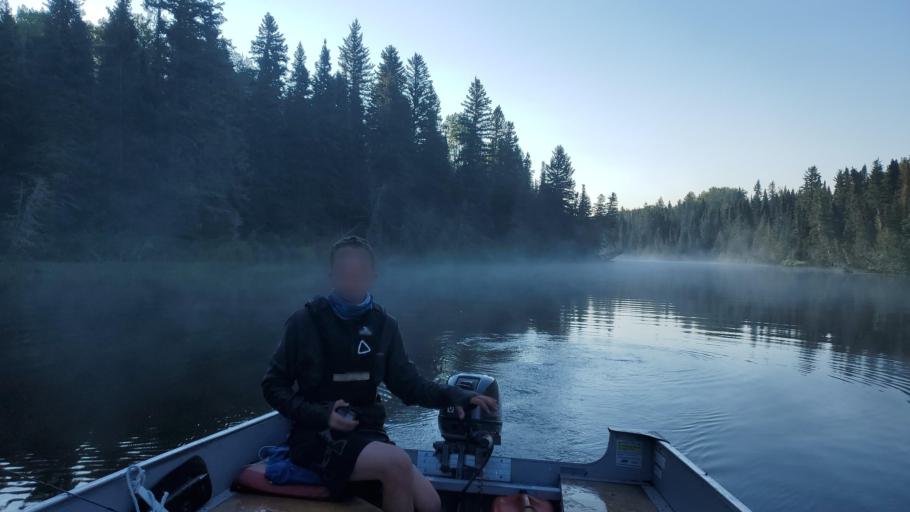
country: CA
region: Ontario
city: Greenstone
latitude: 49.9706
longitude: -87.9021
